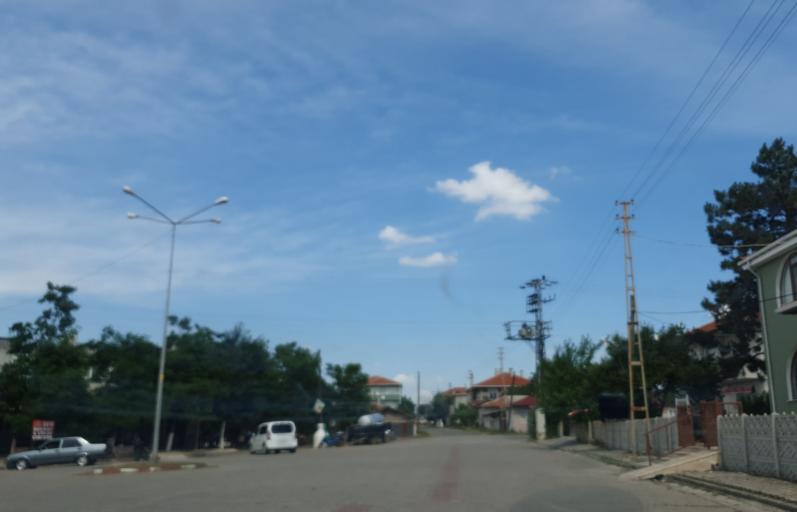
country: TR
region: Tekirdag
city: Muratli
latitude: 41.2176
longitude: 27.5480
